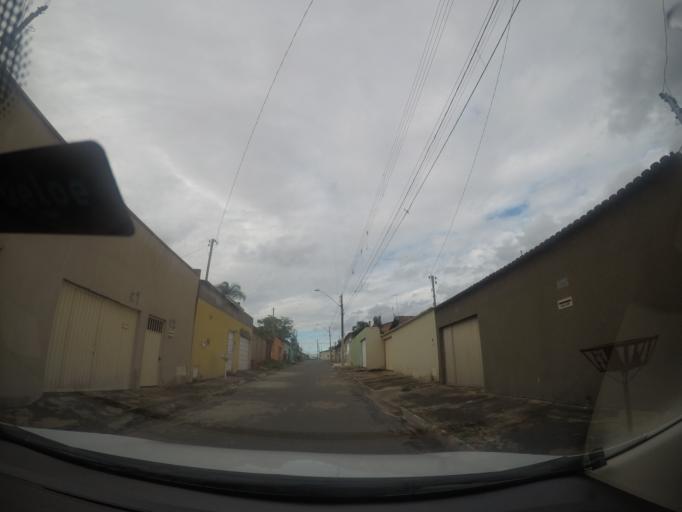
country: BR
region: Goias
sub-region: Goiania
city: Goiania
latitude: -16.6083
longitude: -49.3189
